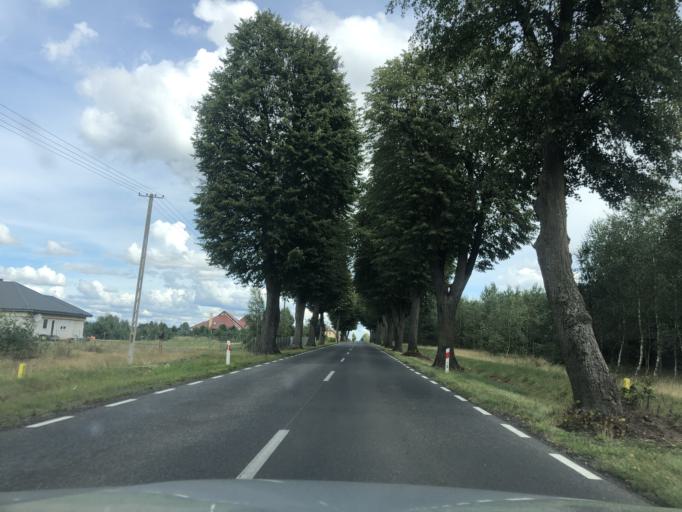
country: PL
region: Greater Poland Voivodeship
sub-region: Powiat czarnkowsko-trzcianecki
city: Trzcianka
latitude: 53.0589
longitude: 16.5138
